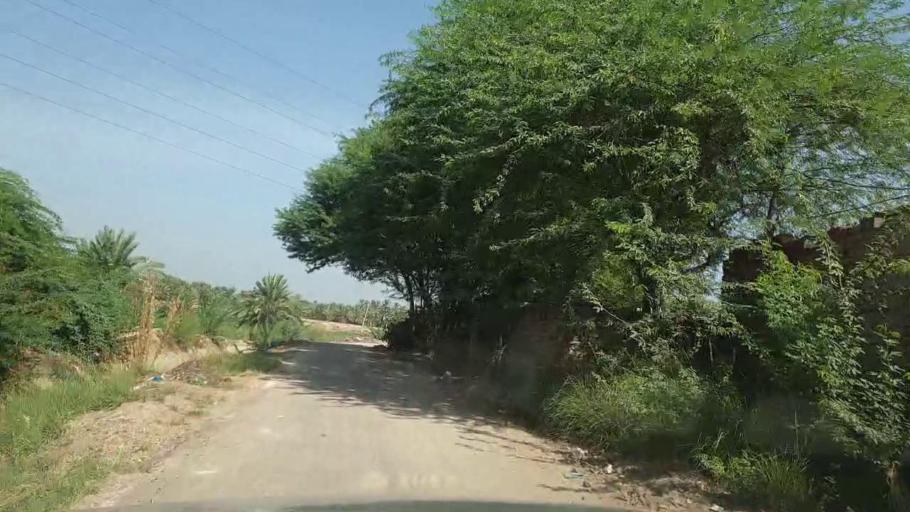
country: PK
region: Sindh
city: Rohri
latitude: 27.6687
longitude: 68.8827
